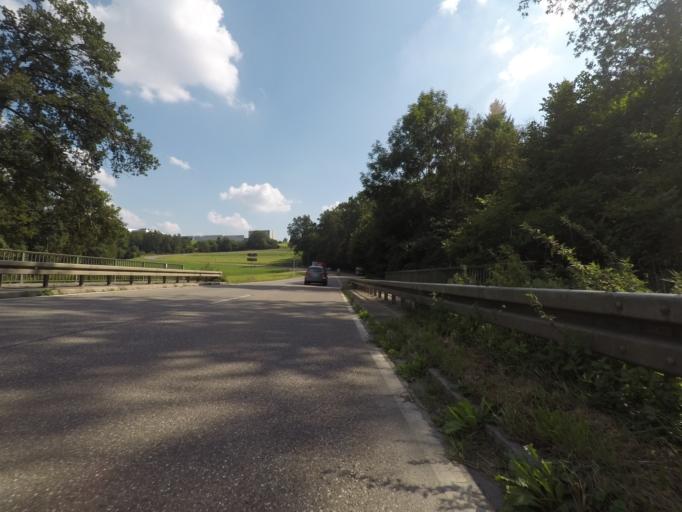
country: DE
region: Baden-Wuerttemberg
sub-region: Regierungsbezirk Stuttgart
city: Ostfildern
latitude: 48.7121
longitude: 9.2395
